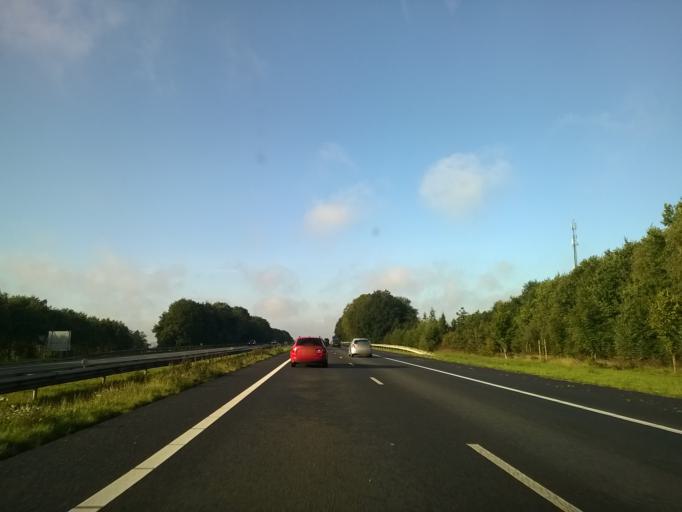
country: NL
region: Groningen
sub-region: Gemeente Leek
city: Leek
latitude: 53.1868
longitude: 6.3831
